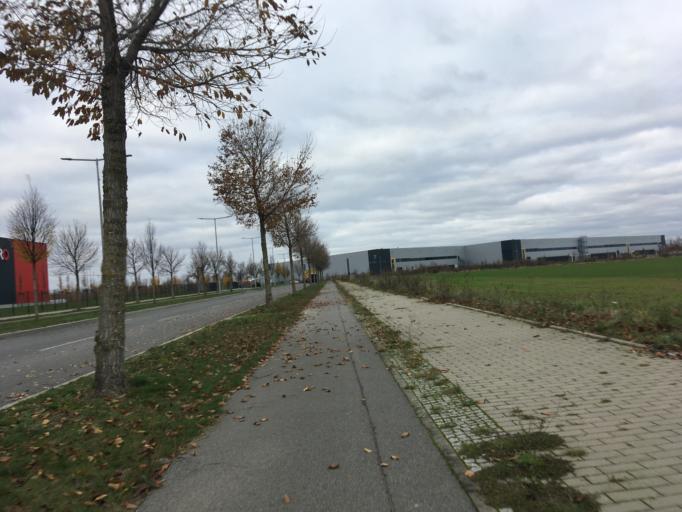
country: DE
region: Berlin
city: Altglienicke
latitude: 52.3898
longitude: 13.5472
